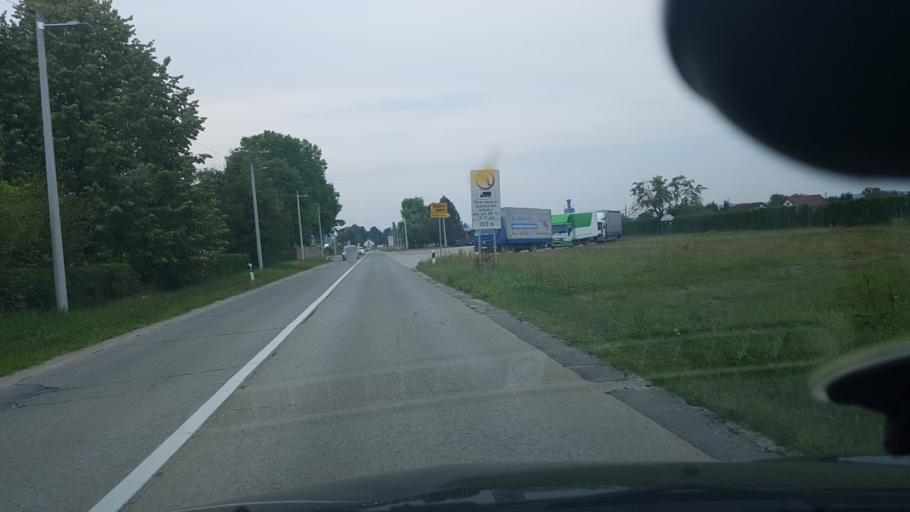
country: HR
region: Zagrebacka
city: Bregana
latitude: 45.8296
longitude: 15.7000
